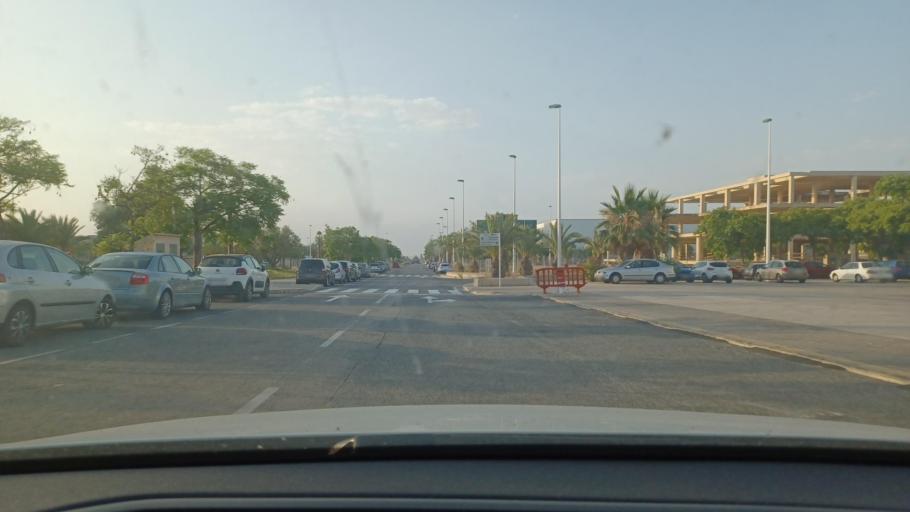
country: ES
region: Valencia
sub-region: Provincia de Alicante
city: Elche
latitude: 38.2908
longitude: -0.6194
